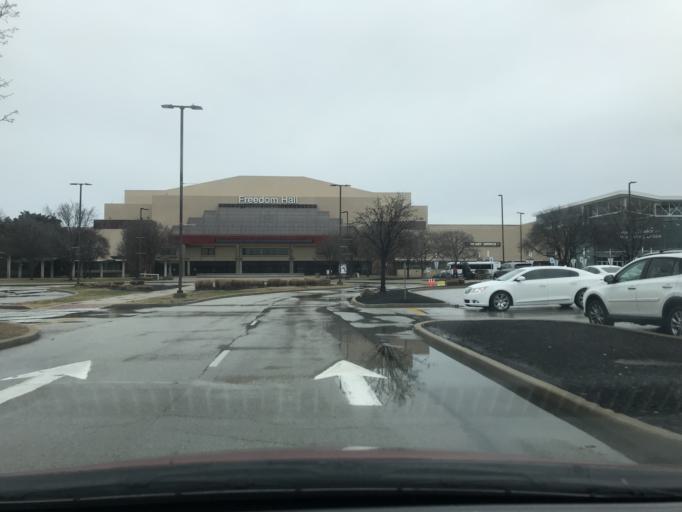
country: US
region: Kentucky
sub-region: Jefferson County
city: Audubon Park
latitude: 38.1983
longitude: -85.7410
